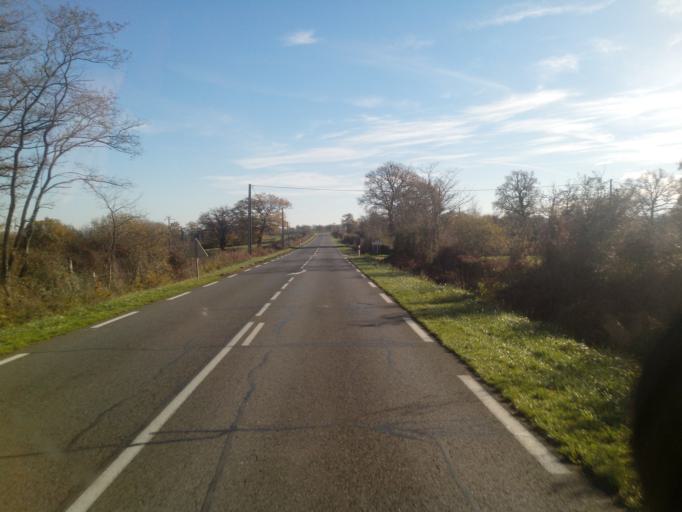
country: FR
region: Limousin
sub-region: Departement de la Haute-Vienne
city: Peyrat-de-Bellac
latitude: 46.1475
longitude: 0.9682
